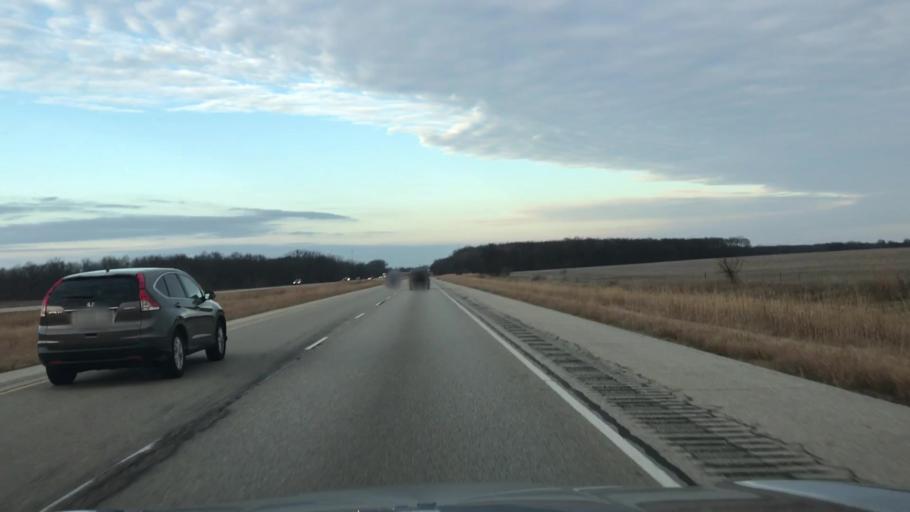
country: US
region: Illinois
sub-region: McLean County
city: Twin Grove
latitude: 40.3658
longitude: -89.1029
